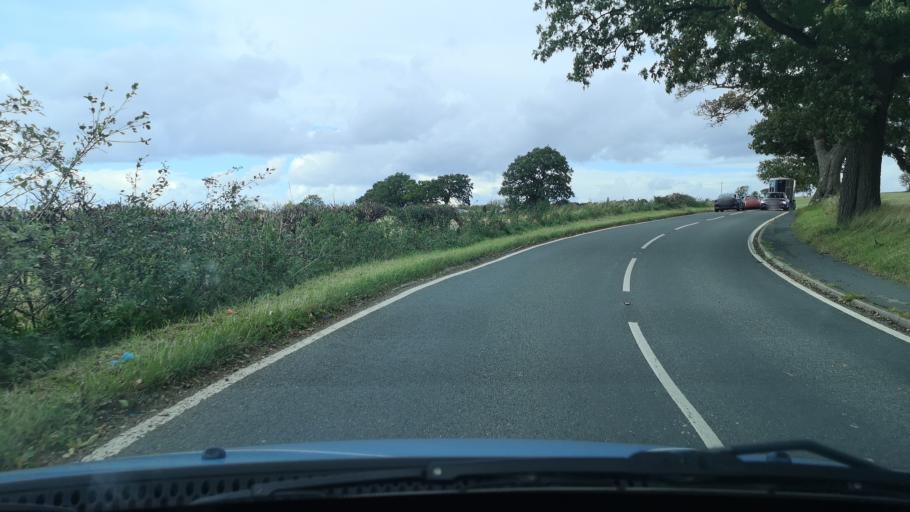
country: GB
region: England
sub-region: City and Borough of Wakefield
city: Featherstone
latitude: 53.6628
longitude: -1.3478
